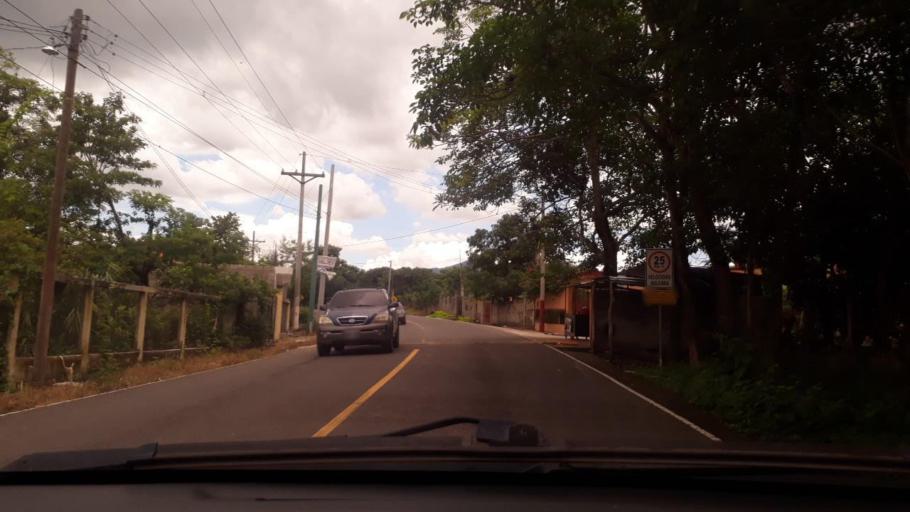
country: GT
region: Jutiapa
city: Jalpatagua
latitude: 14.1331
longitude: -90.0515
